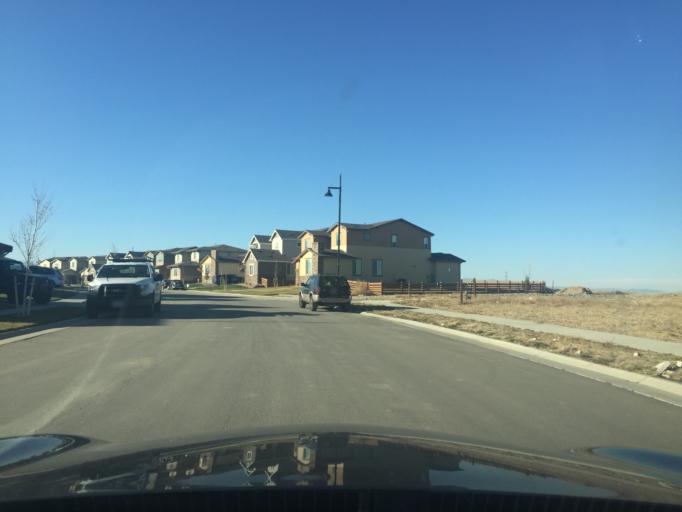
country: US
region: Colorado
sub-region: Boulder County
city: Erie
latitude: 40.0506
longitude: -105.0336
